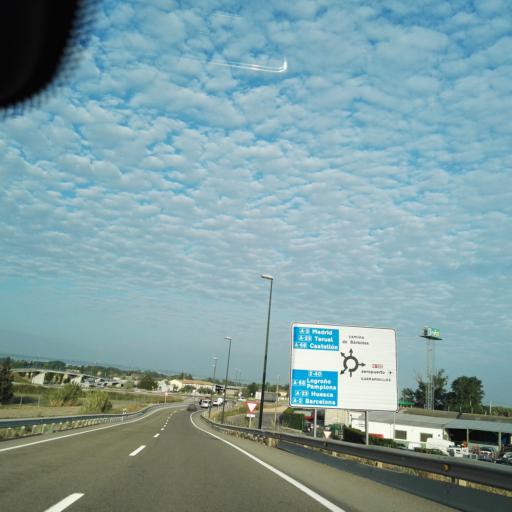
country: ES
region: Aragon
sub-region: Provincia de Zaragoza
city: Oliver-Valdefierro, Oliver, Valdefierro
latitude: 41.6613
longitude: -0.9511
